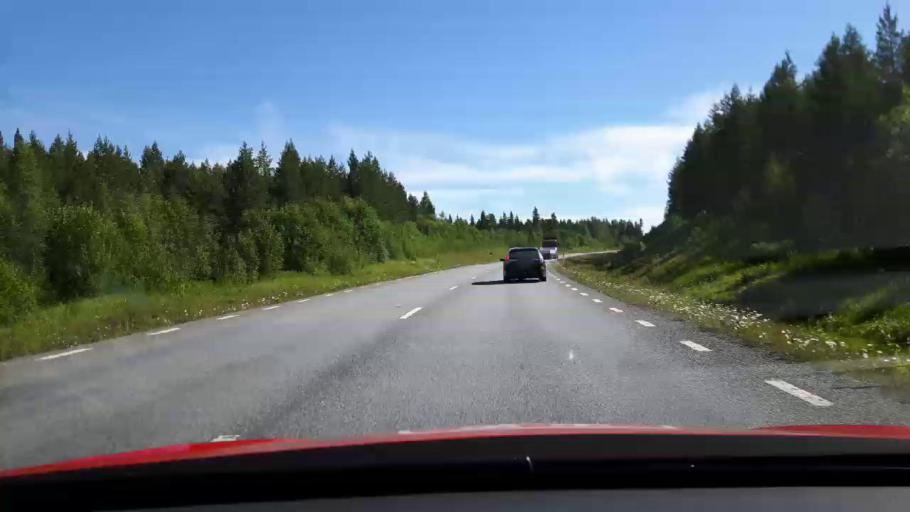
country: SE
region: Jaemtland
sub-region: OEstersunds Kommun
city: Lit
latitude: 63.3870
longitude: 14.8962
